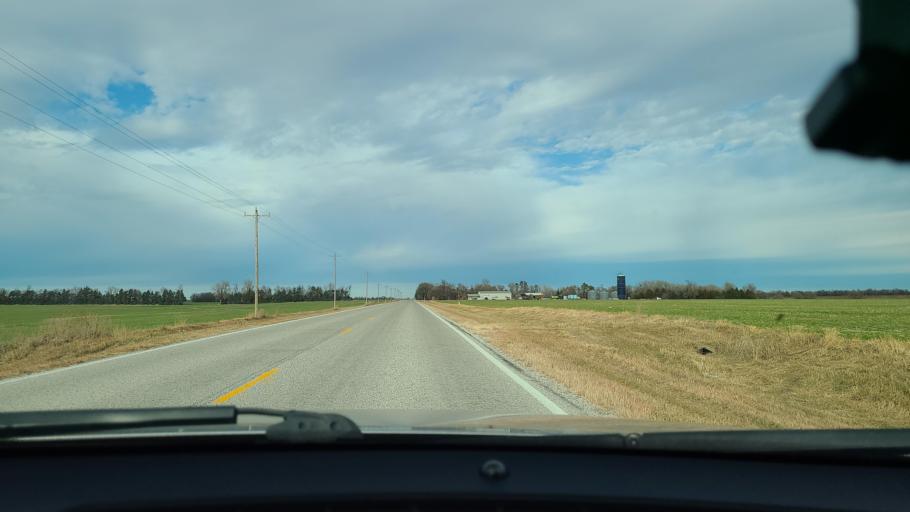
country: US
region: Kansas
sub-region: McPherson County
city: Inman
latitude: 38.3094
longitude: -97.9248
